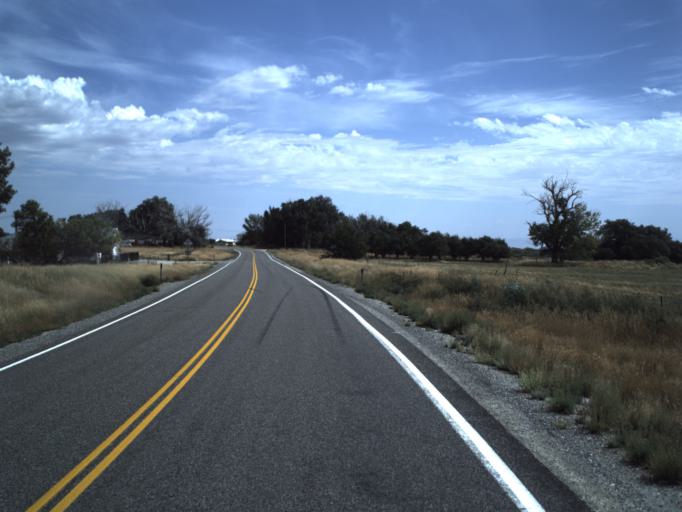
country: US
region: Idaho
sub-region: Cassia County
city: Burley
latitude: 41.8184
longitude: -113.4181
